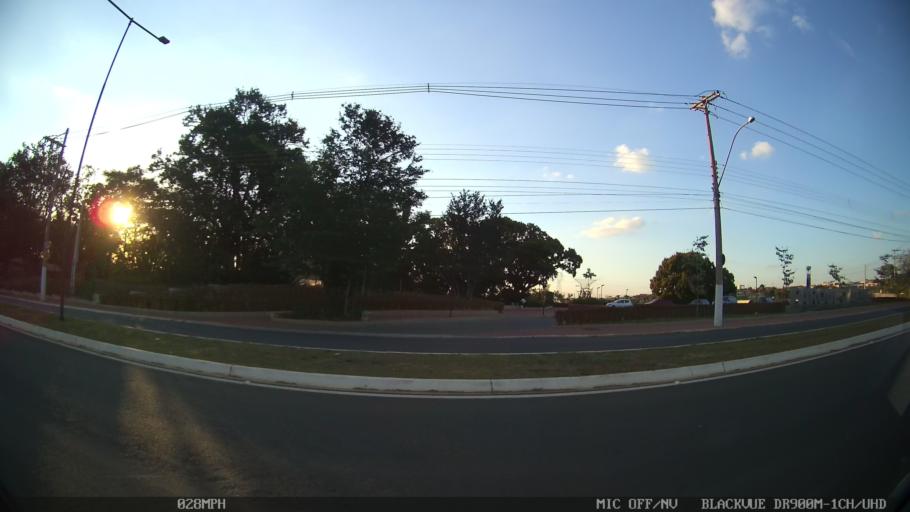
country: BR
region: Sao Paulo
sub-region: Santa Barbara D'Oeste
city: Santa Barbara d'Oeste
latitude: -22.7413
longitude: -47.4035
